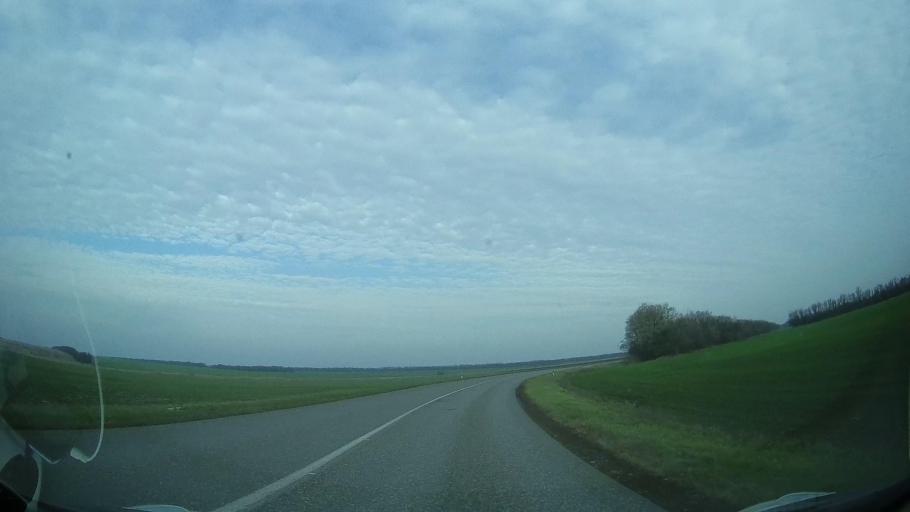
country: RU
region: Rostov
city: Zernograd
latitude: 46.9649
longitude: 40.3680
